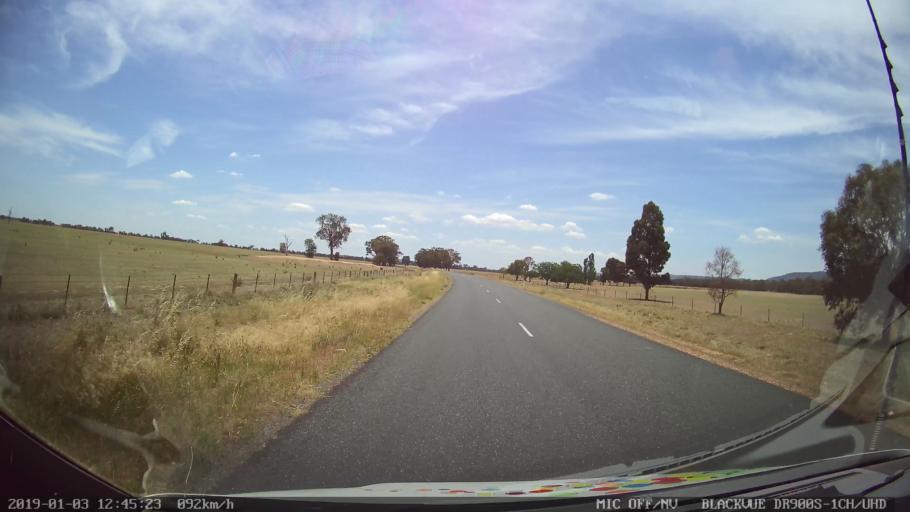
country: AU
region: New South Wales
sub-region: Weddin
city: Grenfell
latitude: -33.7501
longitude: 148.2229
